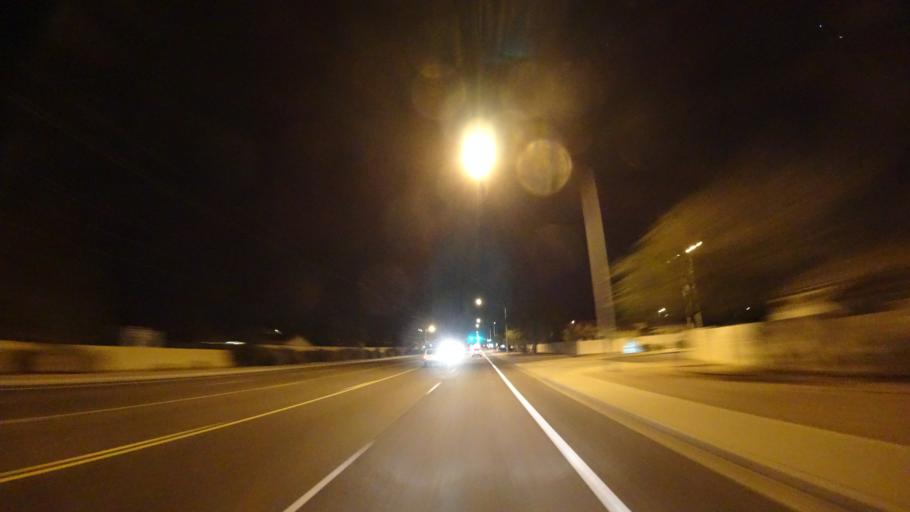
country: US
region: Arizona
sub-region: Maricopa County
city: Mesa
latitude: 33.4372
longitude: -111.7296
